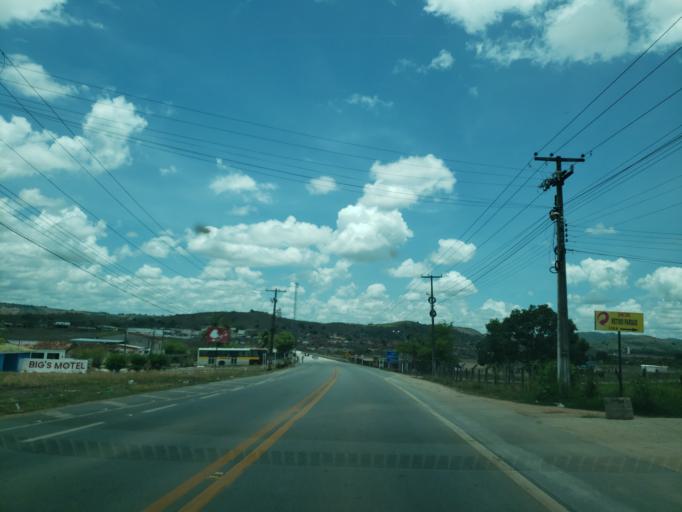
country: BR
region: Alagoas
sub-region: Uniao Dos Palmares
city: Uniao dos Palmares
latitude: -9.1570
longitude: -36.0136
